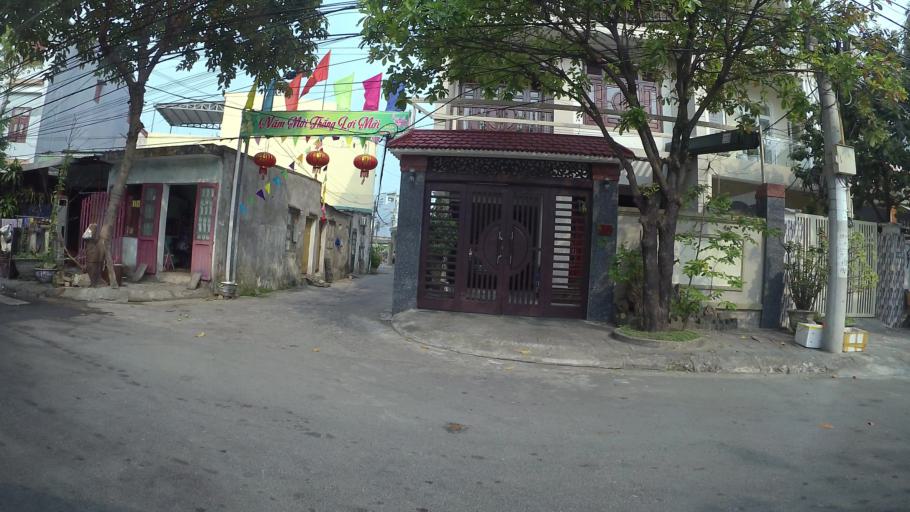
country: VN
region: Da Nang
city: Son Tra
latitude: 16.0930
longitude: 108.2495
